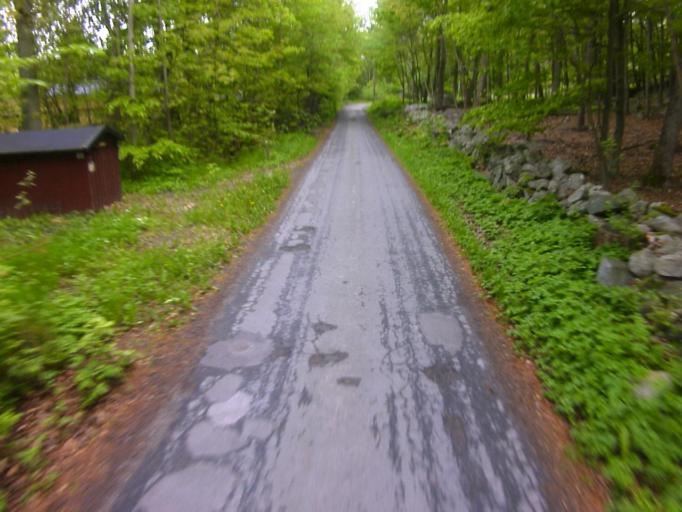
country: SE
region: Blekinge
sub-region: Solvesborgs Kommun
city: Soelvesborg
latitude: 56.0625
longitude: 14.5525
